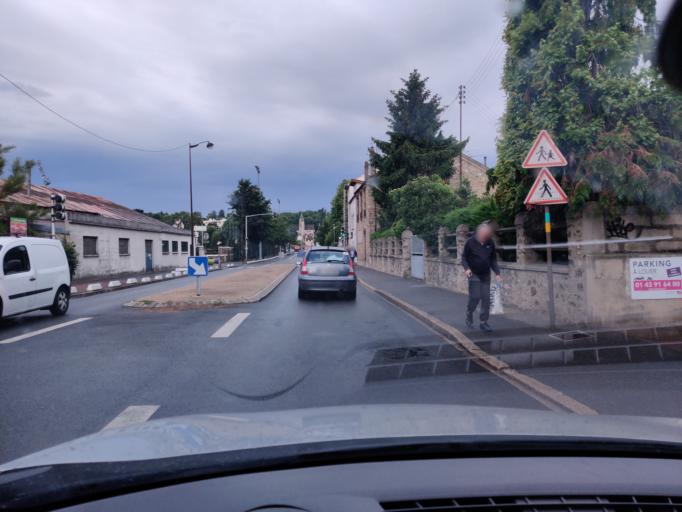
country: FR
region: Ile-de-France
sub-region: Departement de l'Essonne
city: Juvisy-sur-Orge
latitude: 48.6735
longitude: 2.3816
